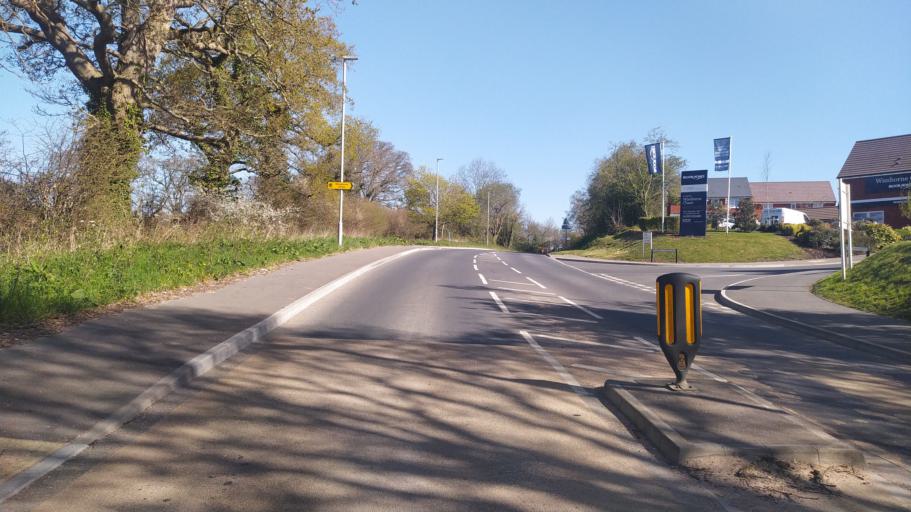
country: GB
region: England
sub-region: Dorset
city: Wimborne Minster
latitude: 50.8093
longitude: -1.9862
